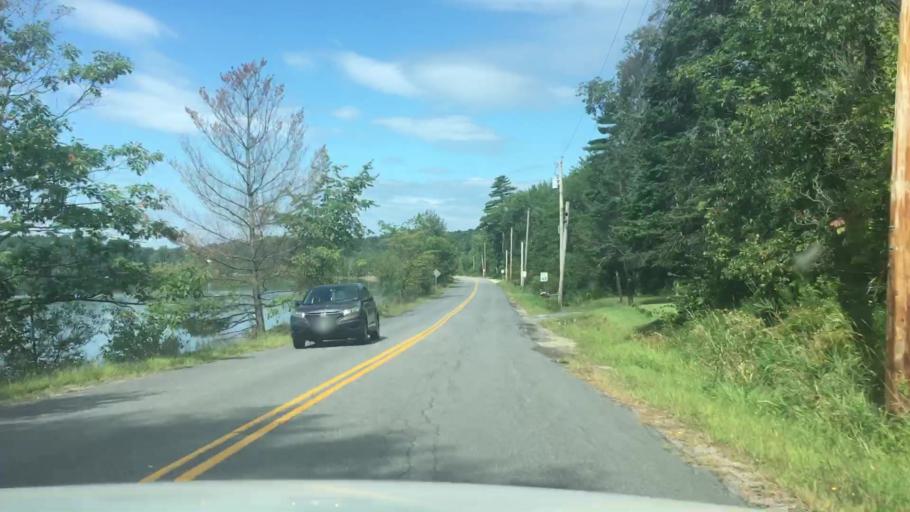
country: US
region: Maine
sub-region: Androscoggin County
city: Auburn
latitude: 44.1570
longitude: -70.2365
